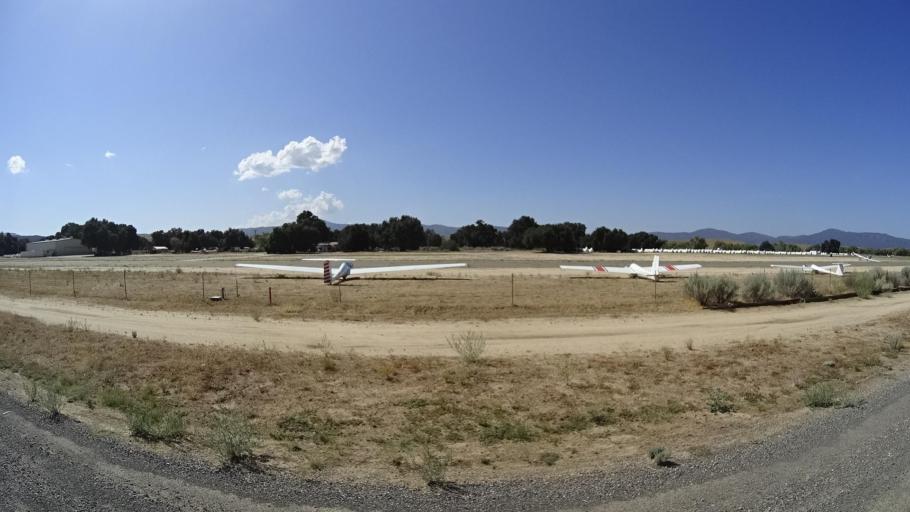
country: US
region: California
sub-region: San Diego County
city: Julian
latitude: 33.2852
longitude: -116.6664
